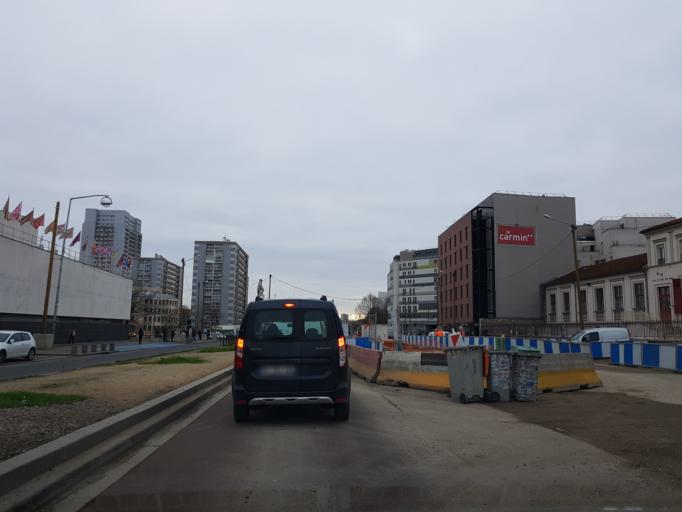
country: FR
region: Ile-de-France
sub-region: Departement du Val-de-Marne
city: Vitry-sur-Seine
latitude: 48.7933
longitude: 2.3859
